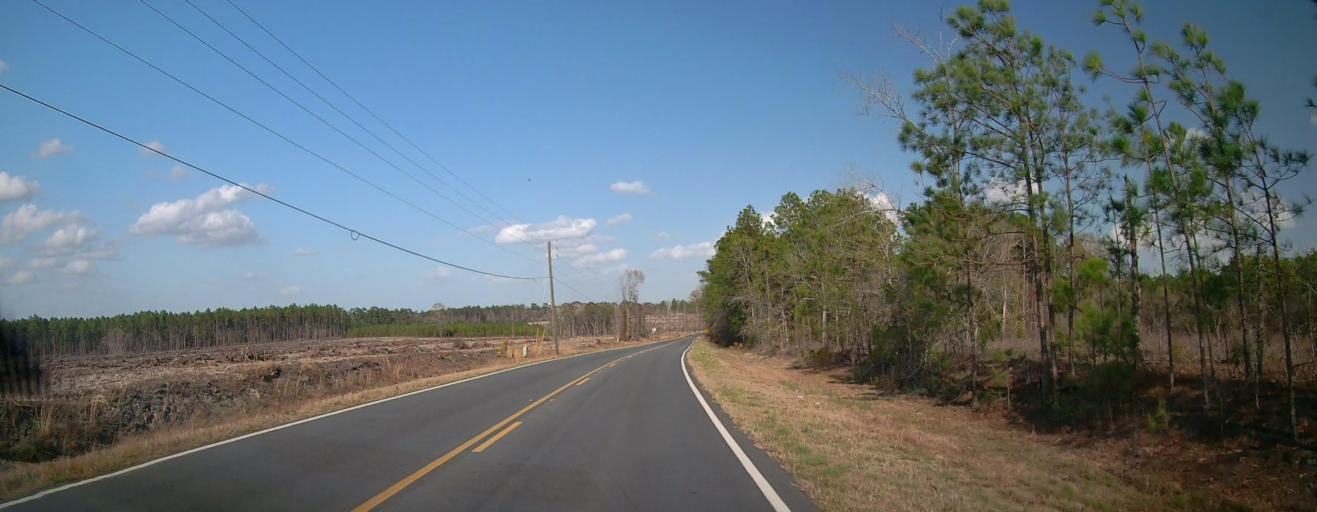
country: US
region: Georgia
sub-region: Telfair County
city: McRae
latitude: 32.0412
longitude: -82.8333
